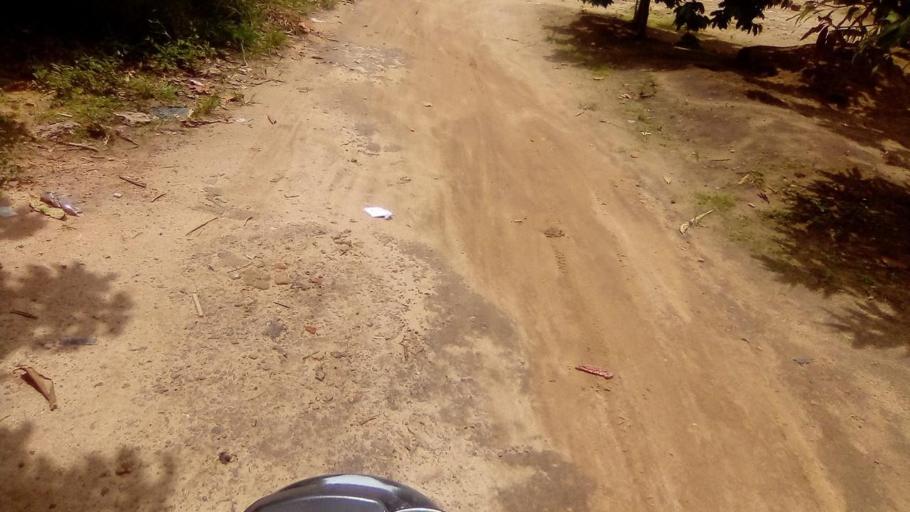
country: SL
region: Southern Province
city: Bo
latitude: 7.9379
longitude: -11.7411
